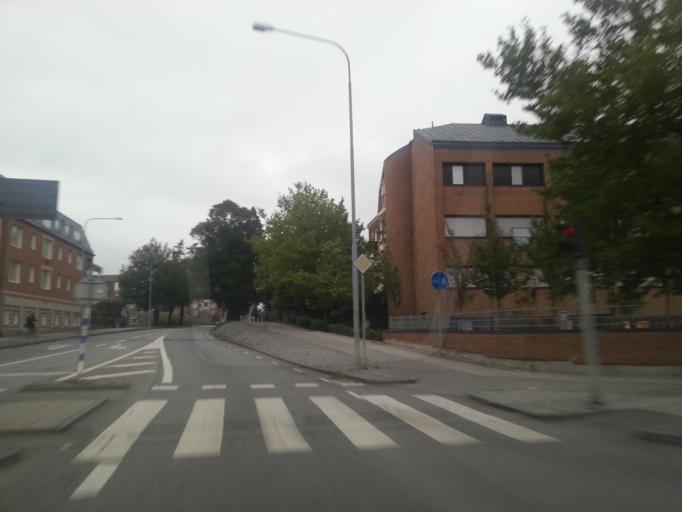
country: SE
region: Skane
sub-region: Trelleborgs Kommun
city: Trelleborg
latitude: 55.3750
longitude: 13.1473
